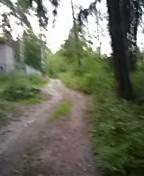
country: RU
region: Moskovskaya
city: Zhukovskiy
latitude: 55.5813
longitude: 38.1138
